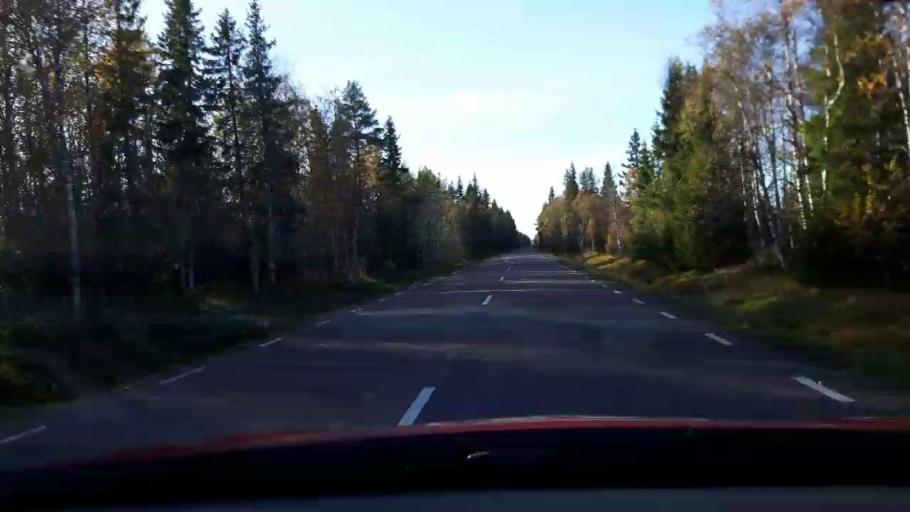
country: SE
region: Jaemtland
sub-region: Stroemsunds Kommun
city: Stroemsund
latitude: 63.8496
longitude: 15.2655
